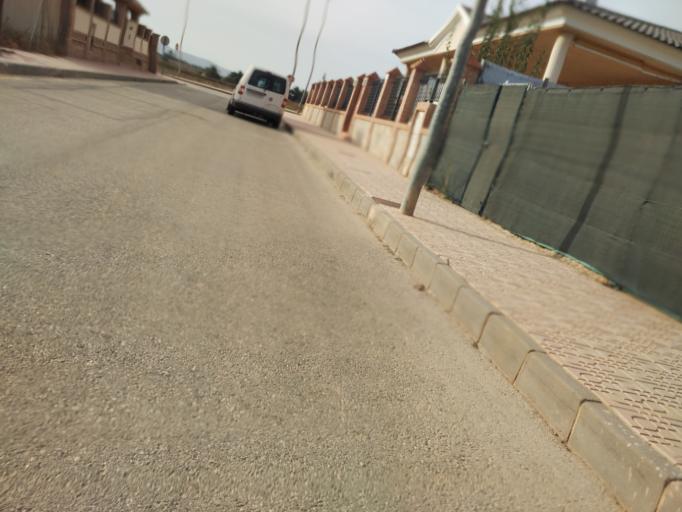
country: ES
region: Murcia
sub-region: Murcia
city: Los Alcazares
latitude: 37.7526
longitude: -0.8532
